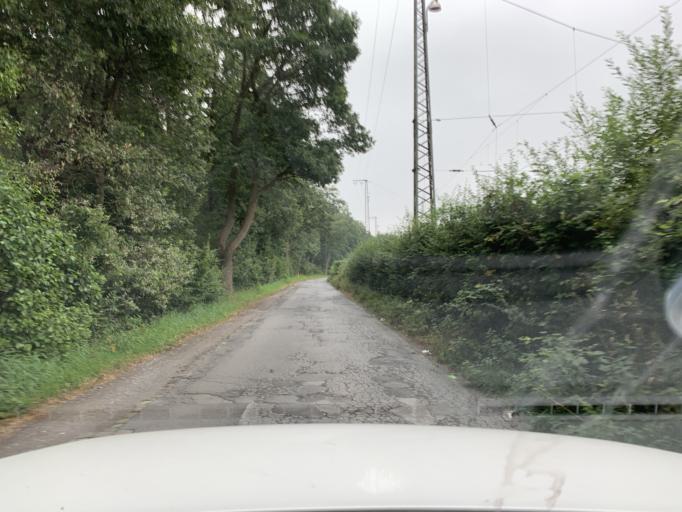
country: DE
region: North Rhine-Westphalia
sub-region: Regierungsbezirk Dusseldorf
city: Hochfeld
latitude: 51.3823
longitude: 6.8131
